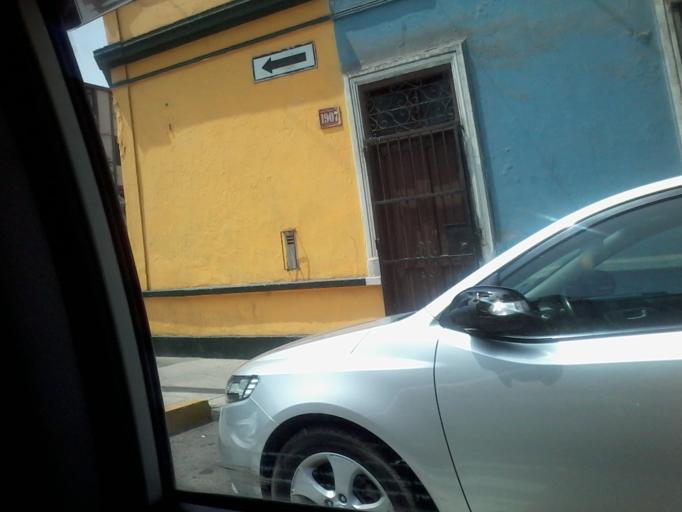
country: PE
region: Lima
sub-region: Lima
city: San Isidro
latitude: -12.0841
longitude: -77.0365
